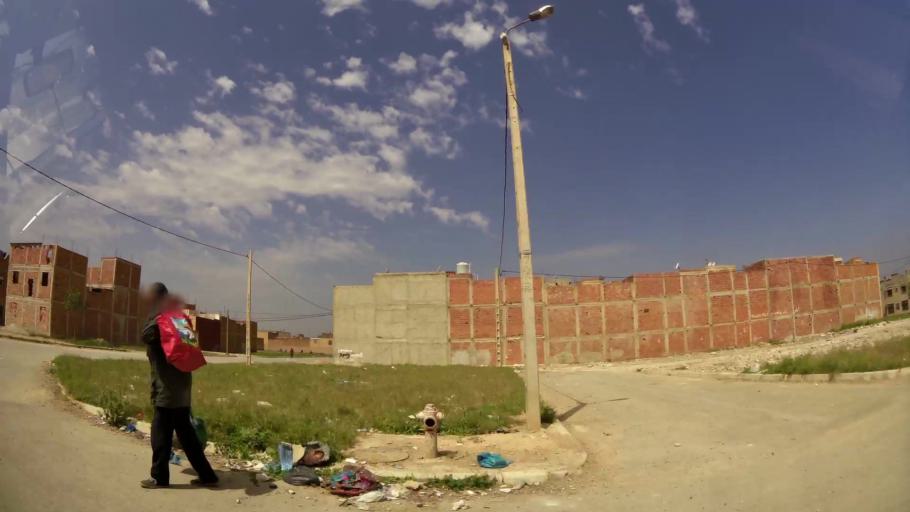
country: MA
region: Oriental
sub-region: Oujda-Angad
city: Oujda
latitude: 34.6815
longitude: -1.8972
